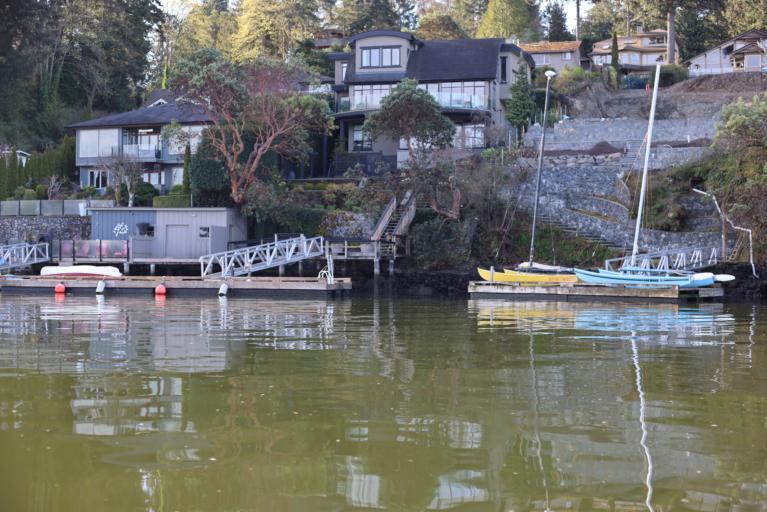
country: CA
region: British Columbia
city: North Saanich
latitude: 48.5713
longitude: -123.4679
